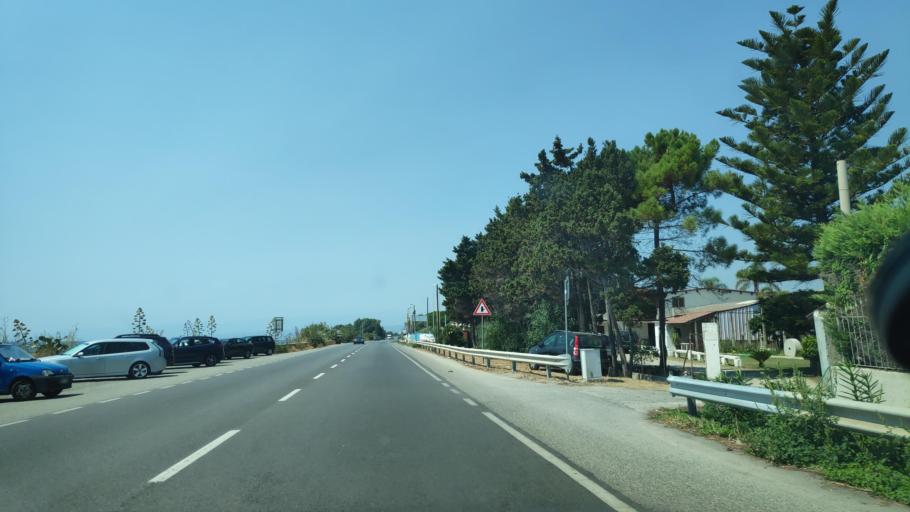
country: IT
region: Calabria
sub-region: Provincia di Reggio Calabria
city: Roccella Ionica
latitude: 38.3123
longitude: 16.3776
